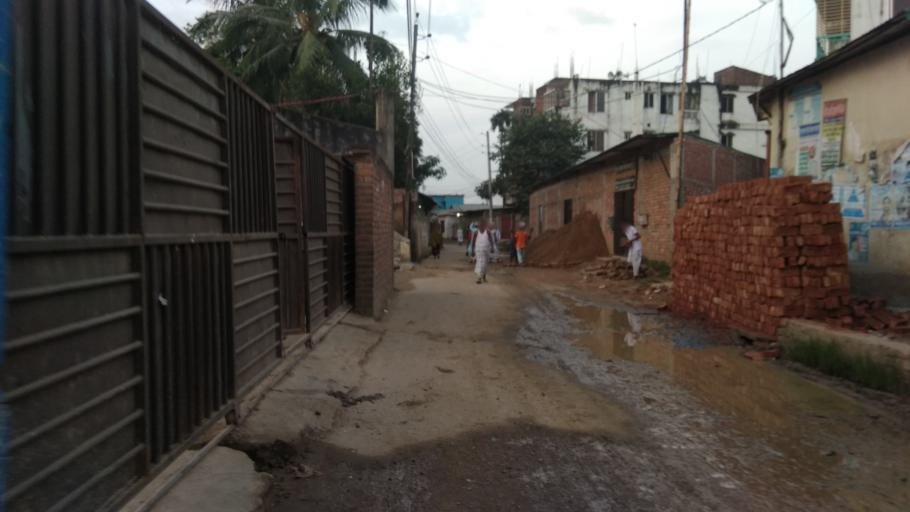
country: BD
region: Dhaka
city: Tungi
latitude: 23.8515
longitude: 90.4257
